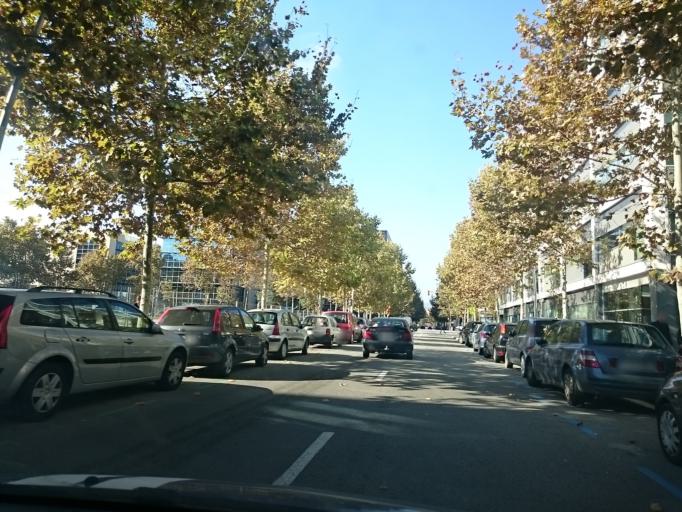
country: ES
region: Catalonia
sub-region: Provincia de Barcelona
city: Sant Marti
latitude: 41.4010
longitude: 2.1992
